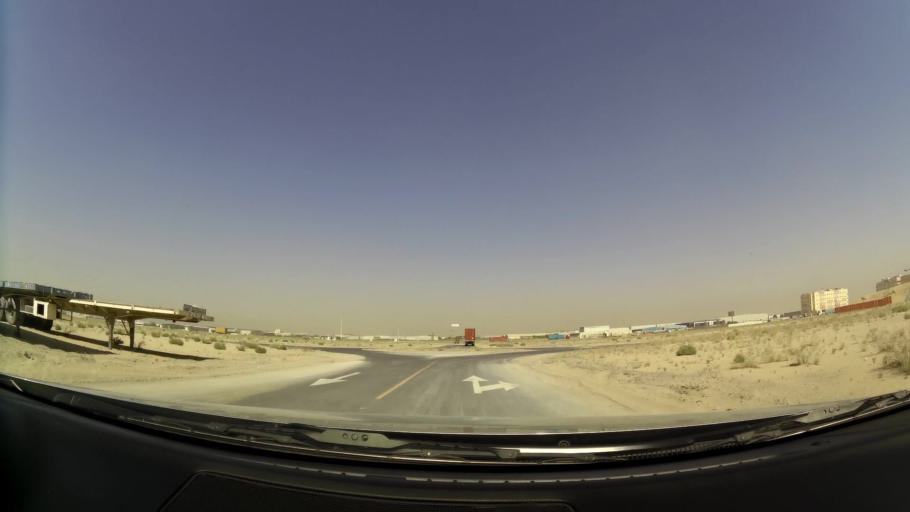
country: AE
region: Dubai
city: Dubai
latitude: 24.9867
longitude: 55.1396
